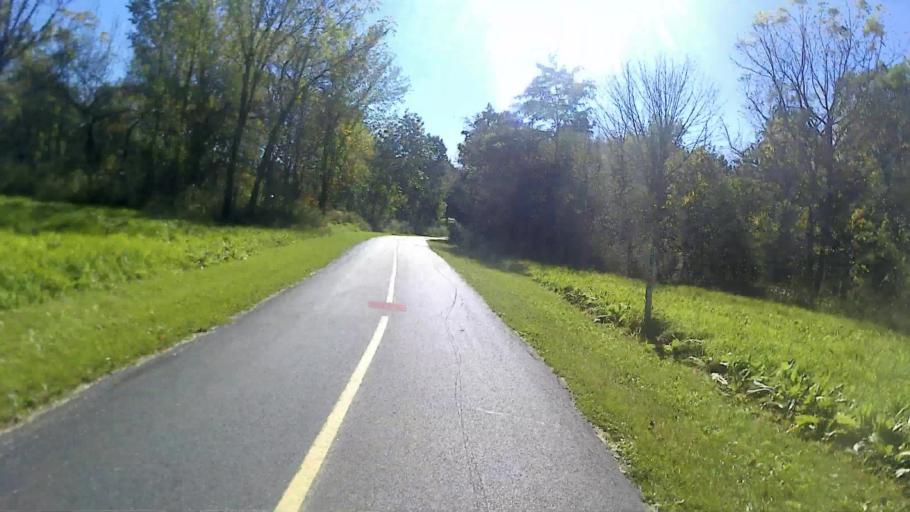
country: US
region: Illinois
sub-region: Cook County
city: Elk Grove Village
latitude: 42.0184
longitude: -87.9923
